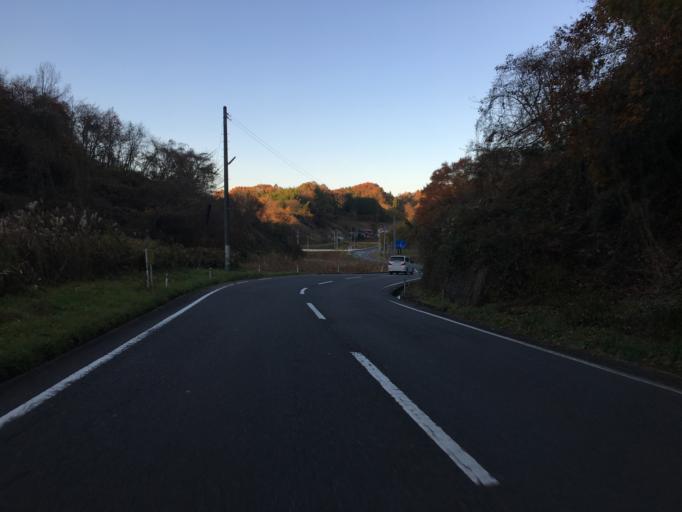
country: JP
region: Fukushima
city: Motomiya
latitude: 37.5255
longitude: 140.4602
